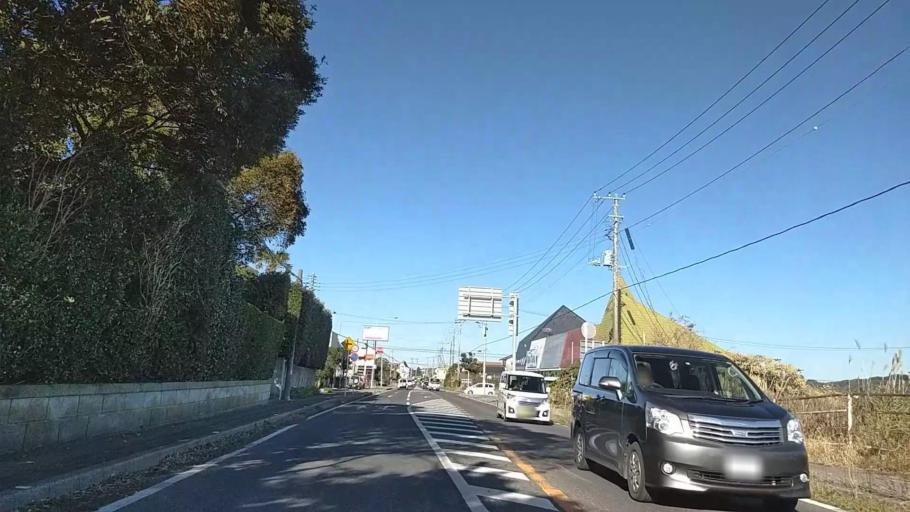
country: JP
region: Chiba
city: Ohara
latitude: 35.2931
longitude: 140.3953
